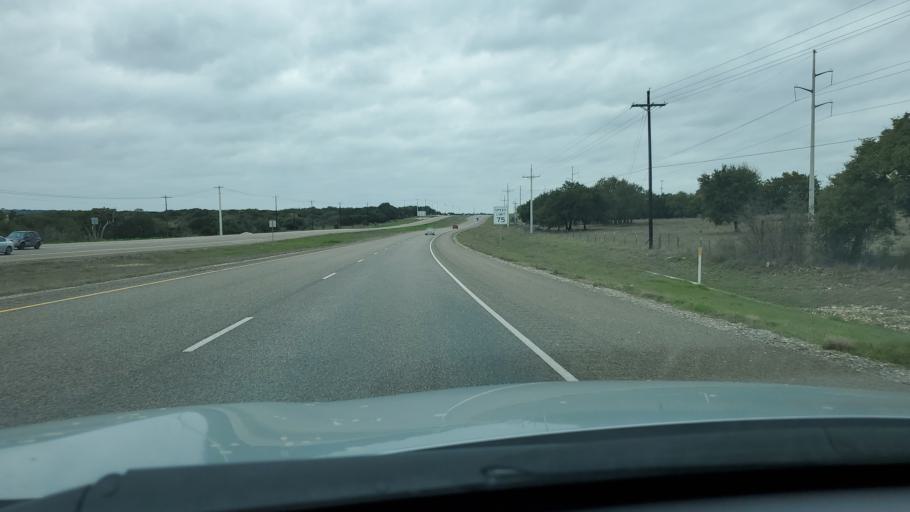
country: US
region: Texas
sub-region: Williamson County
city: Serenada
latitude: 30.7597
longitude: -97.7333
